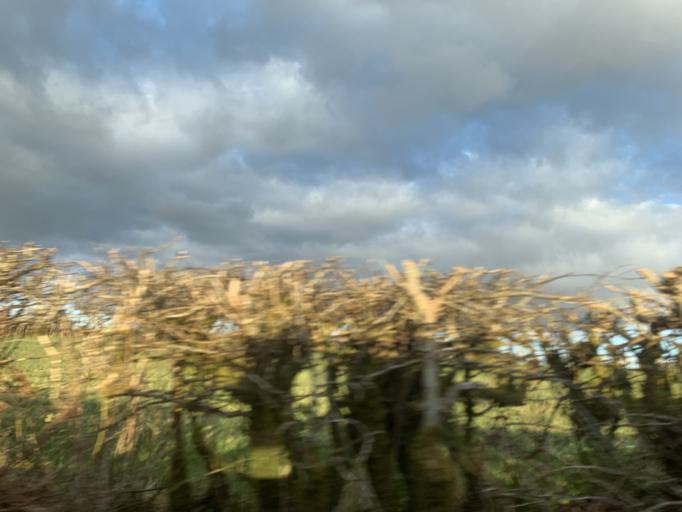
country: IE
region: Connaught
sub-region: Maigh Eo
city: Ballyhaunis
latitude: 53.8227
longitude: -8.7001
